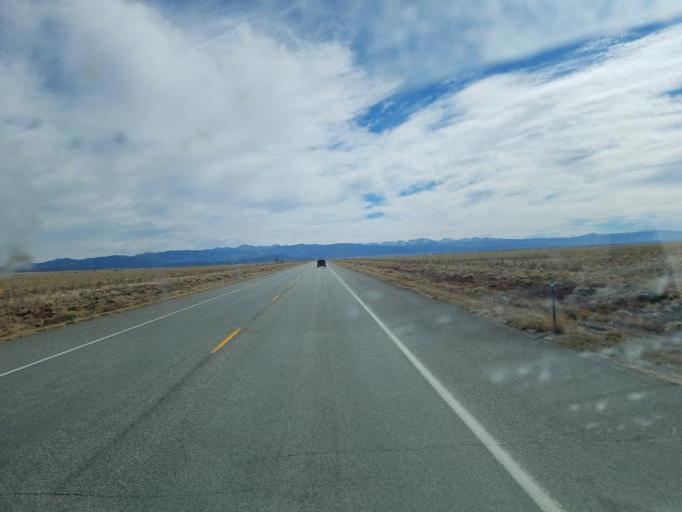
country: US
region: Colorado
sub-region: Alamosa County
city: Alamosa East
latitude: 37.4708
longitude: -105.5783
